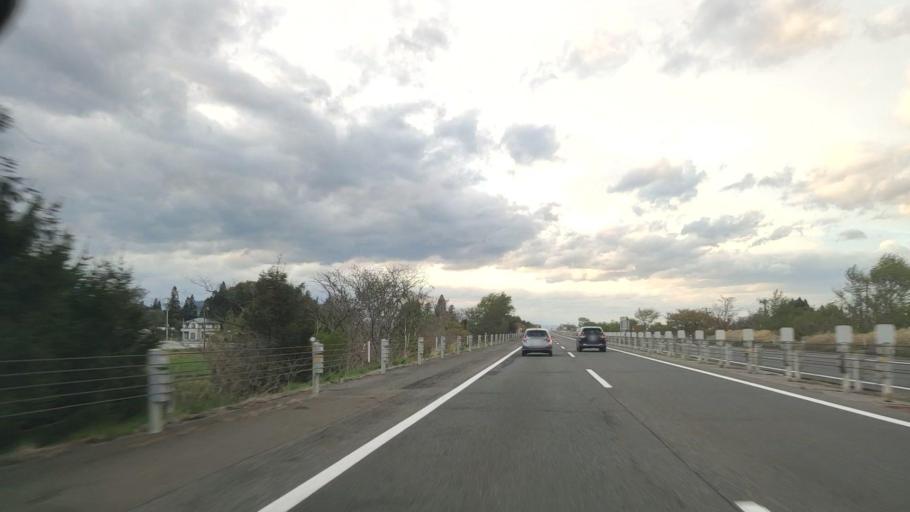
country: JP
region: Iwate
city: Morioka-shi
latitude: 39.6280
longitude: 141.1282
